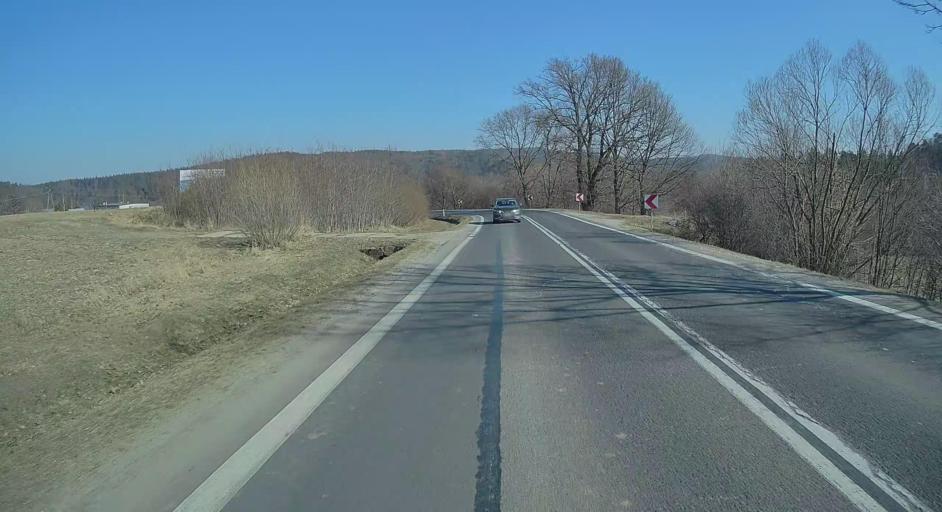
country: PL
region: Subcarpathian Voivodeship
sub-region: Powiat przemyski
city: Bircza
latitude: 49.6552
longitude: 22.4274
